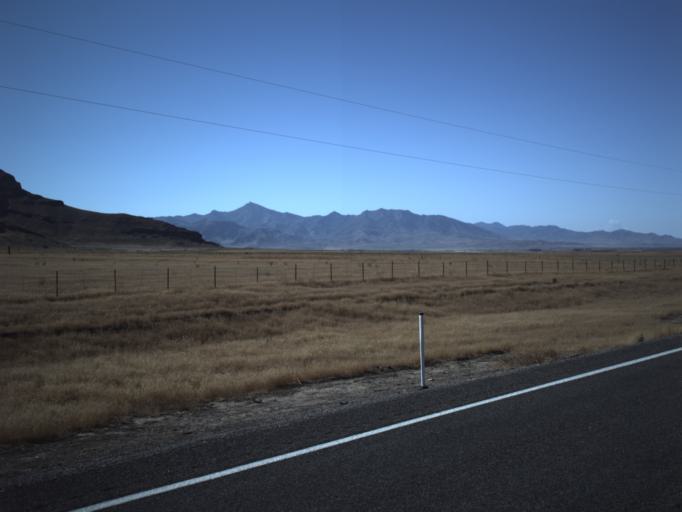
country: US
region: Utah
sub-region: Millard County
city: Delta
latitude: 39.6130
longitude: -112.3186
